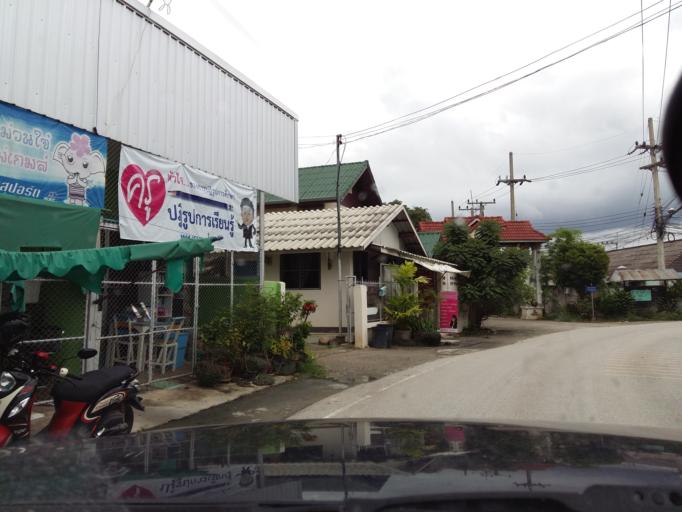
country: TH
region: Chiang Mai
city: Chiang Mai
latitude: 18.7540
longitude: 98.9762
